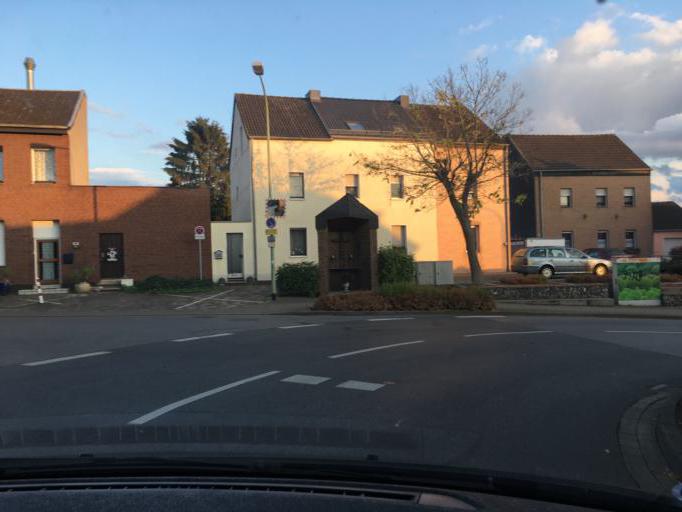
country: DE
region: North Rhine-Westphalia
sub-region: Regierungsbezirk Koln
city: Niederzier
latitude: 50.8529
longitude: 6.4594
